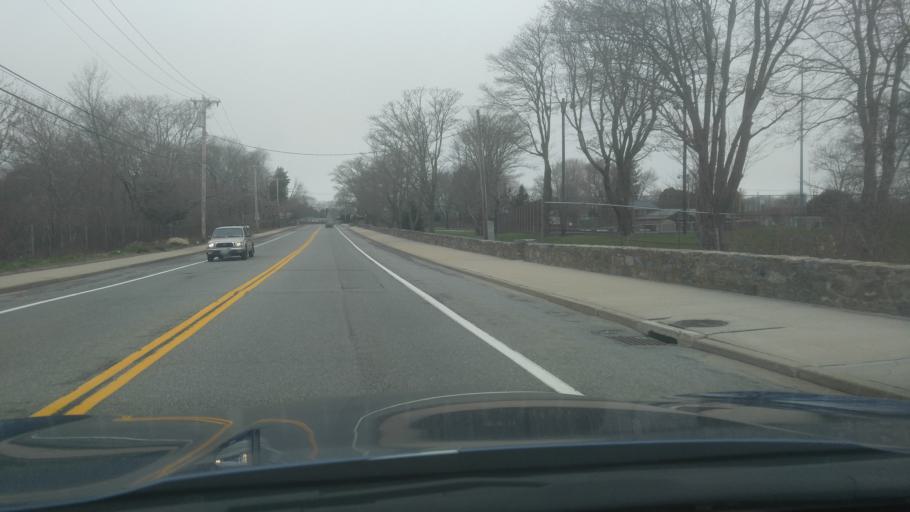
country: US
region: Rhode Island
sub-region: Washington County
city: Narragansett Pier
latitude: 41.4342
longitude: -71.4699
